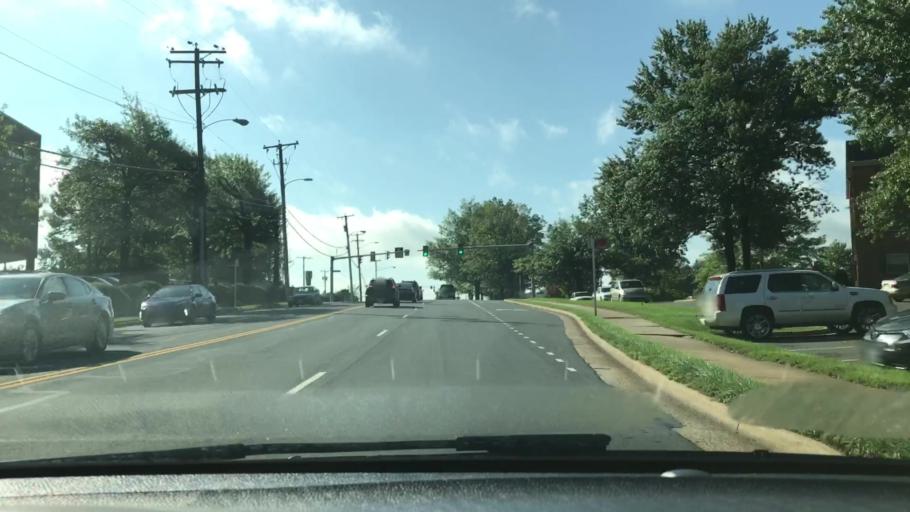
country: US
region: Virginia
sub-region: Fairfax County
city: Annandale
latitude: 38.8342
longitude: -77.1975
